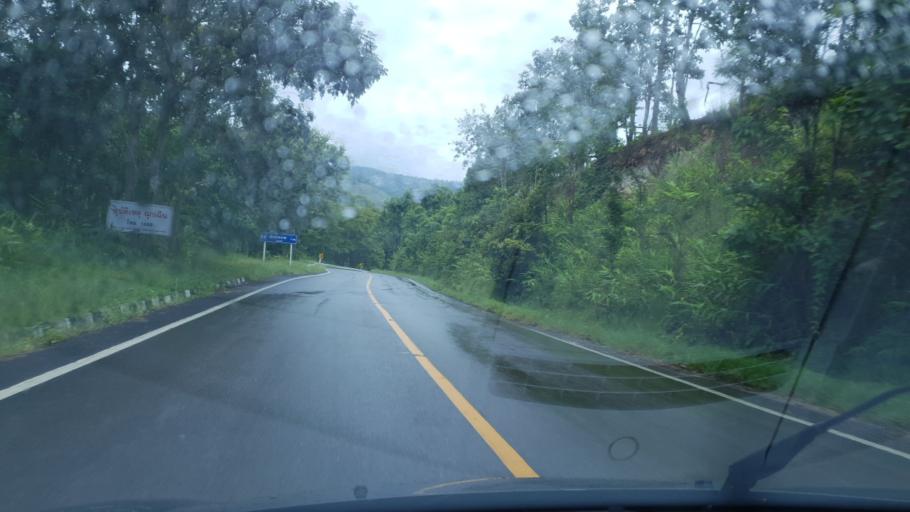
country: TH
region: Mae Hong Son
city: Mae La Noi
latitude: 18.5435
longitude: 97.9377
